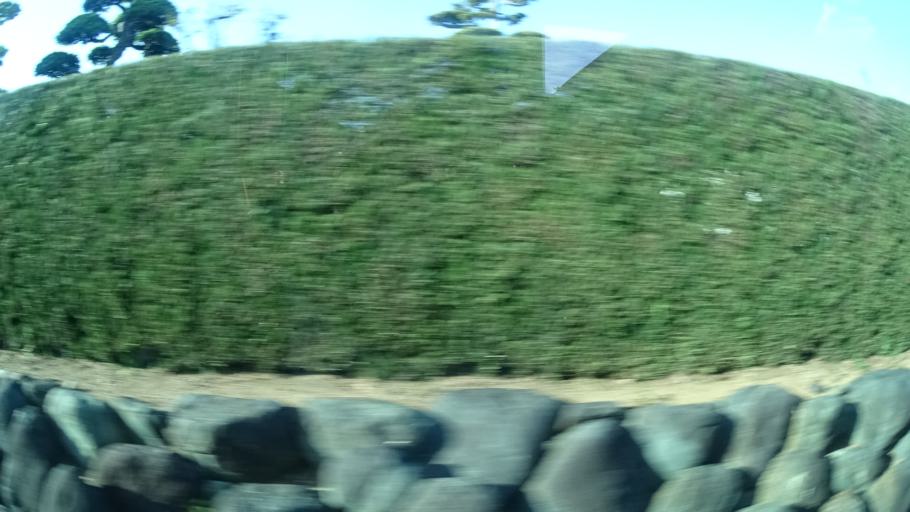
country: JP
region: Aichi
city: Tahara
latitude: 34.6560
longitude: 137.2036
